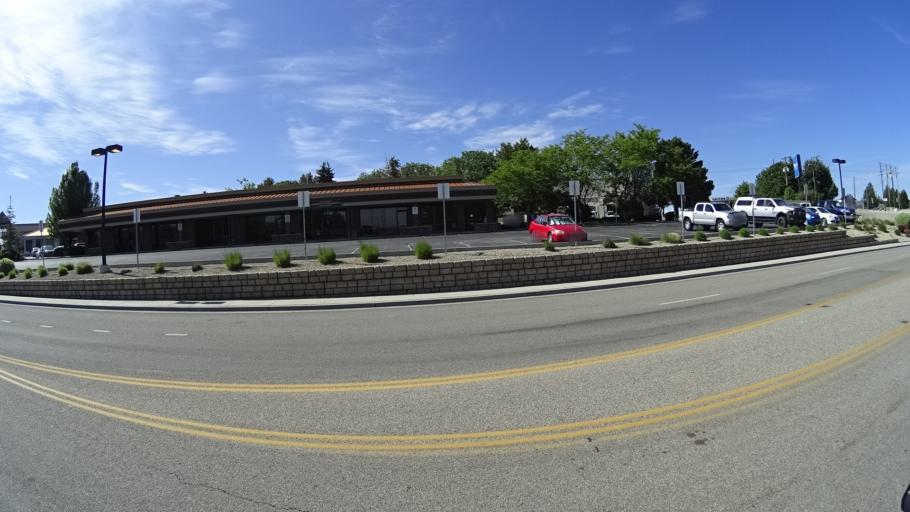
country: US
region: Idaho
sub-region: Ada County
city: Boise
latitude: 43.5694
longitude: -116.2158
